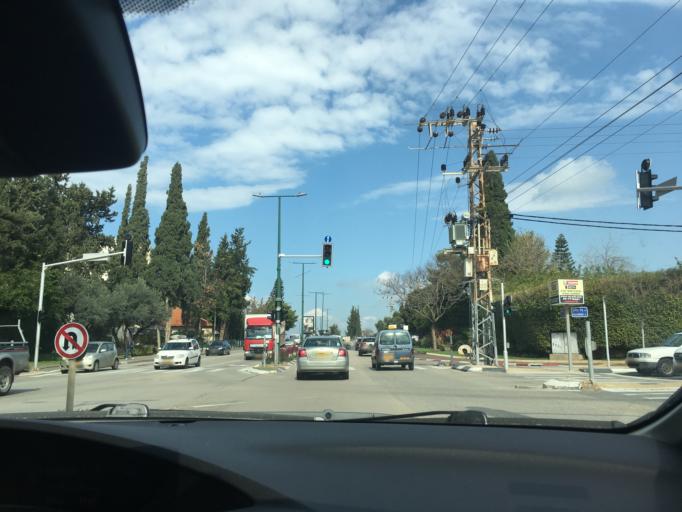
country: IL
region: Central District
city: Ra'anana
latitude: 32.1688
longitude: 34.8529
